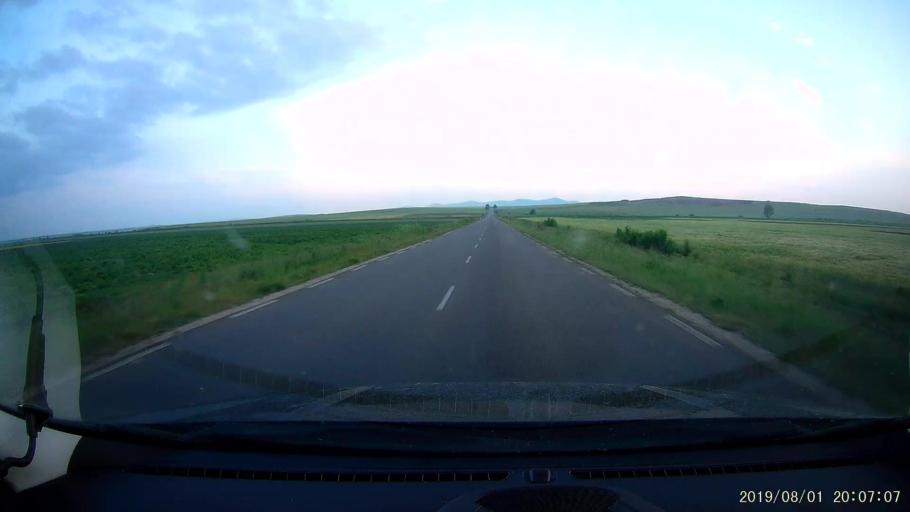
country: BG
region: Yambol
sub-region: Obshtina Yambol
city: Yambol
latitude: 42.5267
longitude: 26.5634
